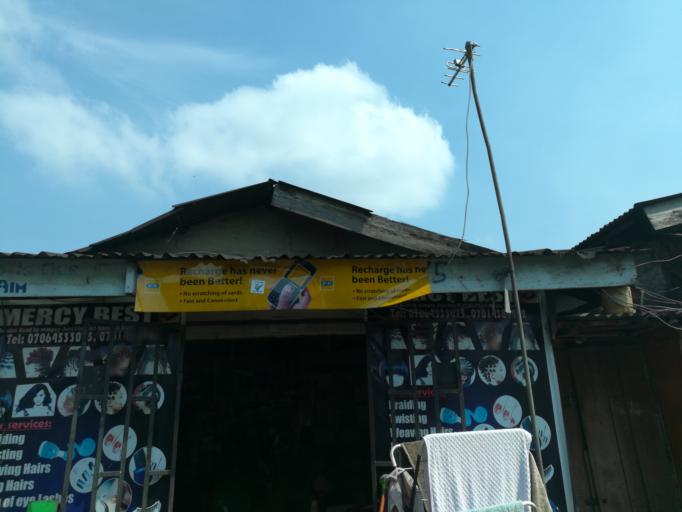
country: NG
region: Rivers
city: Port Harcourt
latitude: 4.8296
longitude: 6.9822
